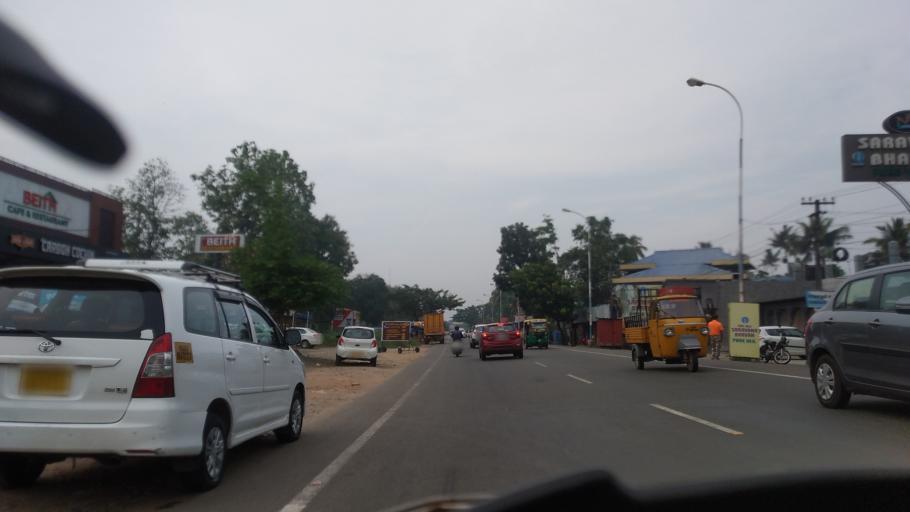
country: IN
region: Kerala
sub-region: Ernakulam
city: Elur
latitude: 10.0452
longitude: 76.2978
